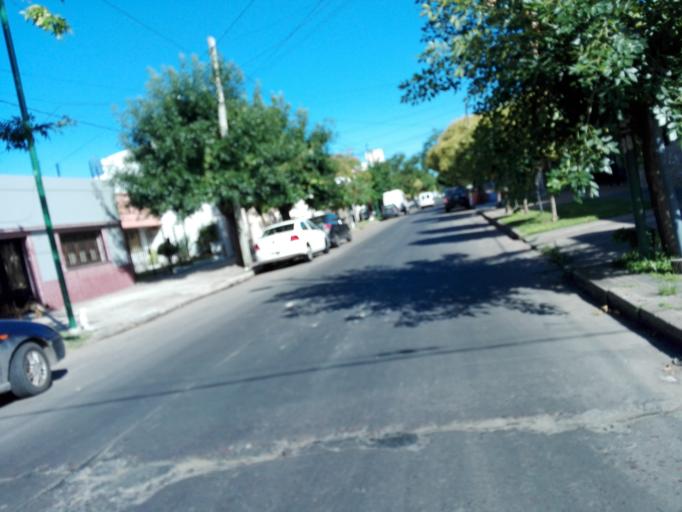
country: AR
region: Buenos Aires
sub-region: Partido de La Plata
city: La Plata
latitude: -34.9413
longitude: -57.9599
